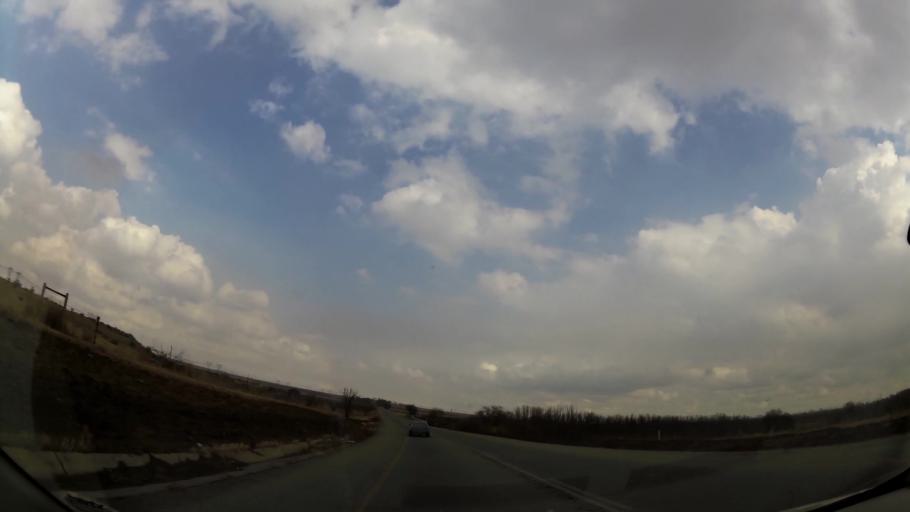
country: ZA
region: Orange Free State
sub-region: Fezile Dabi District Municipality
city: Sasolburg
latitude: -26.8016
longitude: 27.9134
